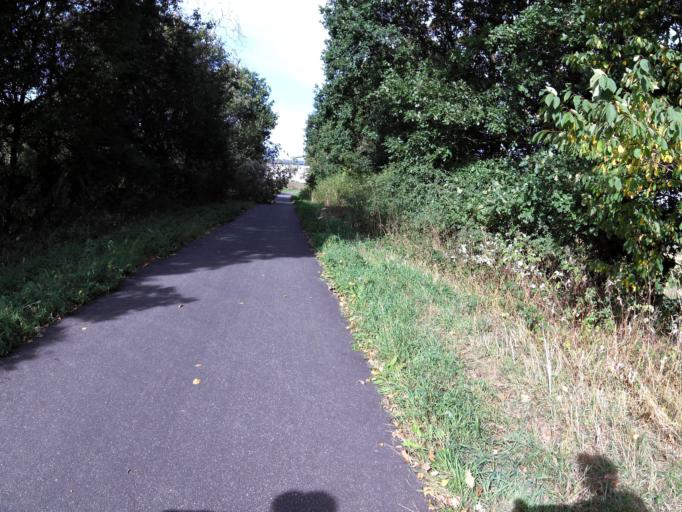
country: DE
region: Rheinland-Pfalz
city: Bleialf
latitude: 50.2255
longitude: 6.2695
